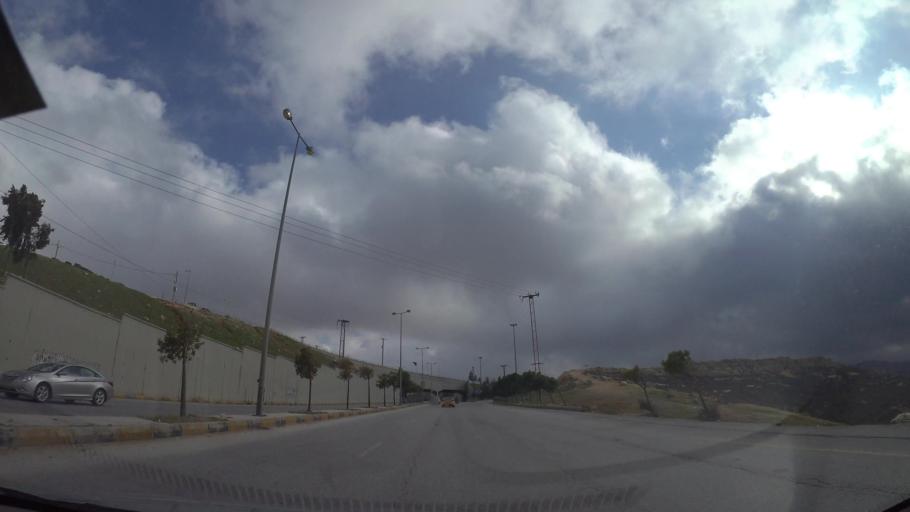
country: JO
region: Amman
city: Al Jubayhah
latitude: 32.0481
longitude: 35.8711
